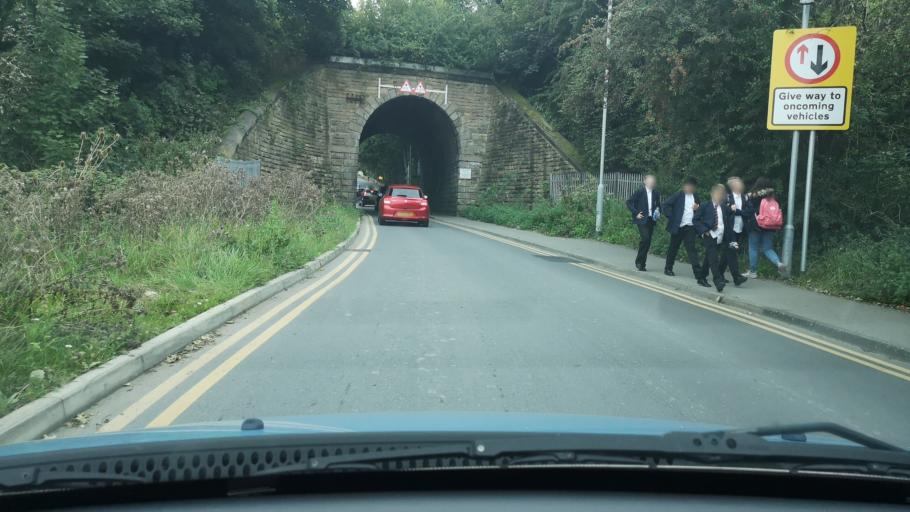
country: GB
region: England
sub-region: City and Borough of Wakefield
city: Pontefract
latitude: 53.6969
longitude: -1.3119
